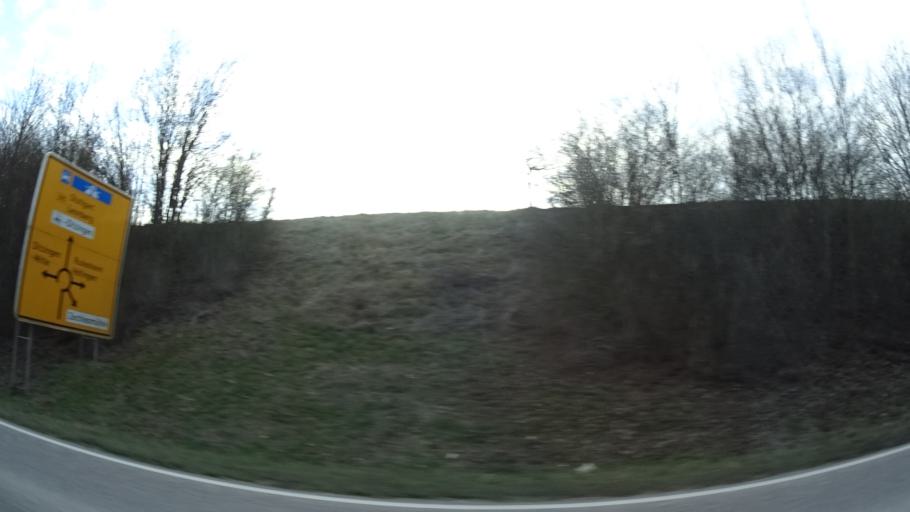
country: DE
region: Baden-Wuerttemberg
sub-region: Regierungsbezirk Stuttgart
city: Ditzingen
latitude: 48.8238
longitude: 9.0538
